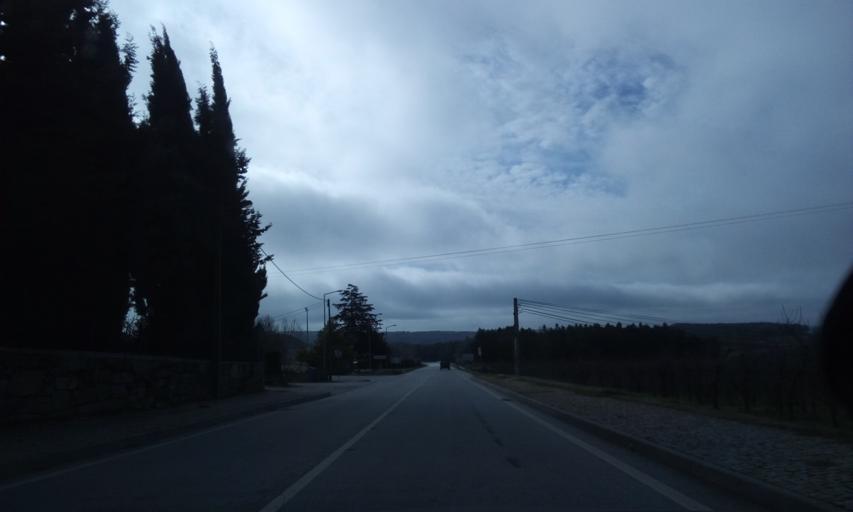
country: PT
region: Guarda
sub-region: Aguiar da Beira
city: Aguiar da Beira
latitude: 40.8165
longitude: -7.5376
